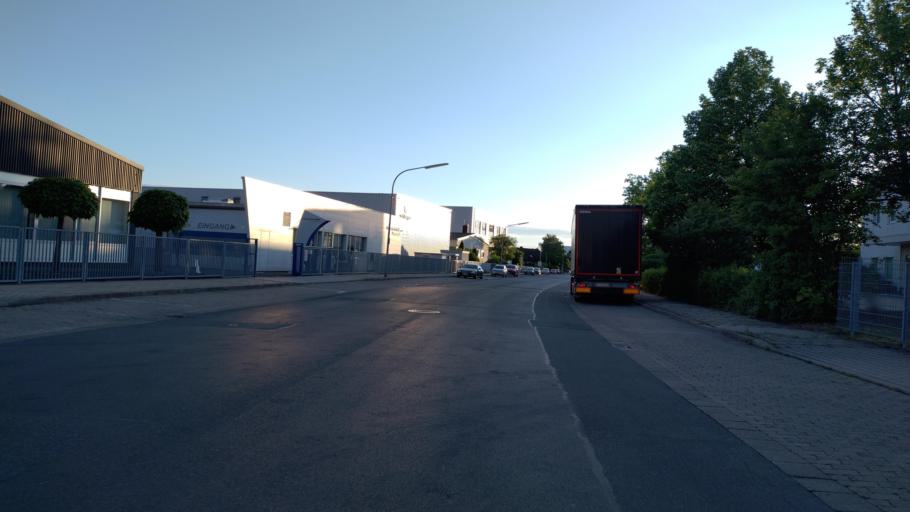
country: DE
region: Bavaria
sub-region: Upper Franconia
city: Bindlach
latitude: 49.9616
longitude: 11.6169
